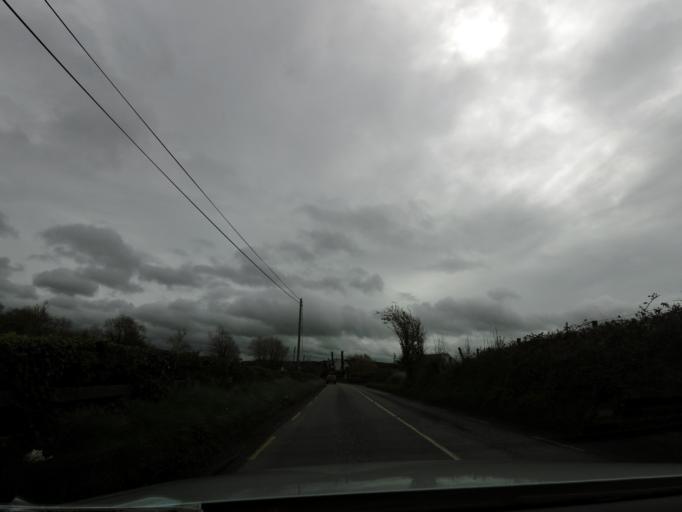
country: IE
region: Leinster
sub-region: Kilkenny
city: Ballyragget
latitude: 52.7314
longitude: -7.3893
